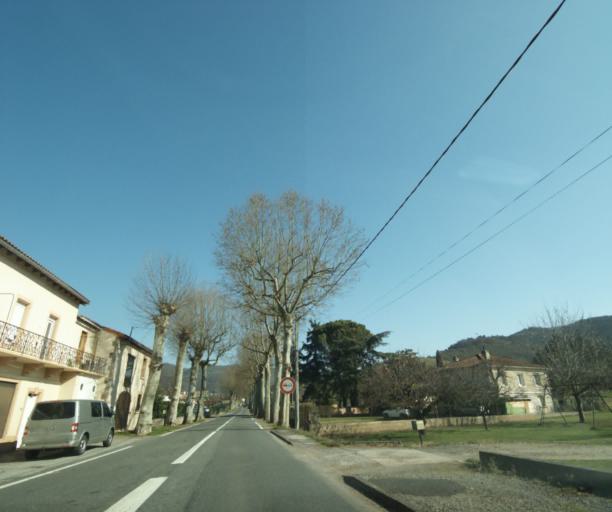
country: FR
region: Midi-Pyrenees
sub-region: Departement de l'Aveyron
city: Saint-Affrique
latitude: 43.9474
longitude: 2.8395
